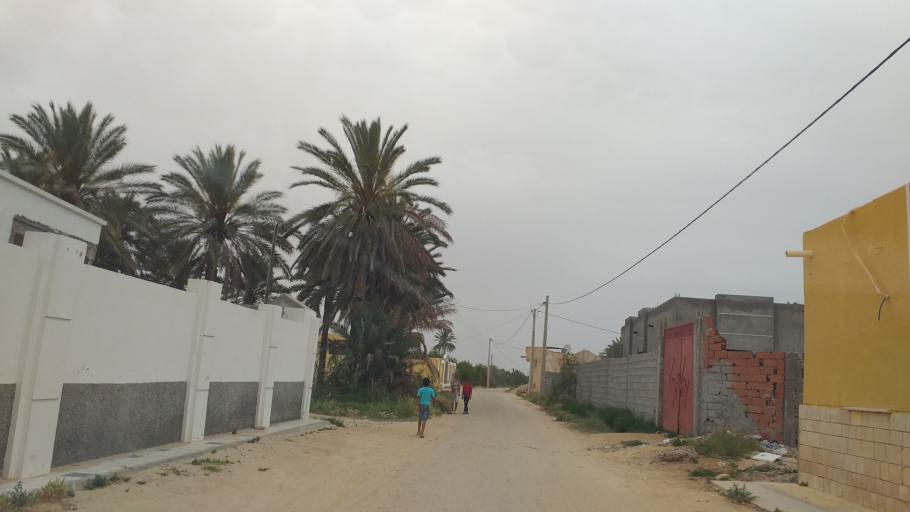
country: TN
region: Qabis
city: Gabes
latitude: 33.9498
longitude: 10.0610
